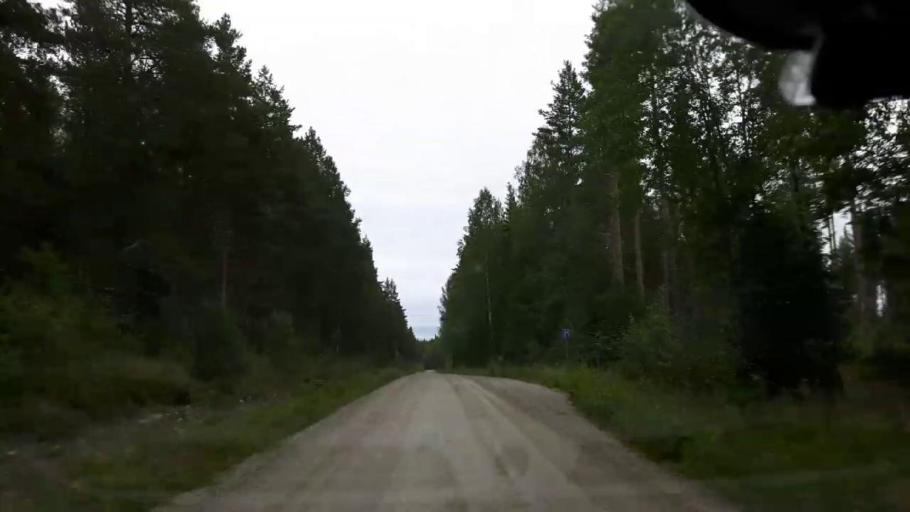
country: SE
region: Jaemtland
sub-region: Braecke Kommun
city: Braecke
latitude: 62.8279
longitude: 15.6976
